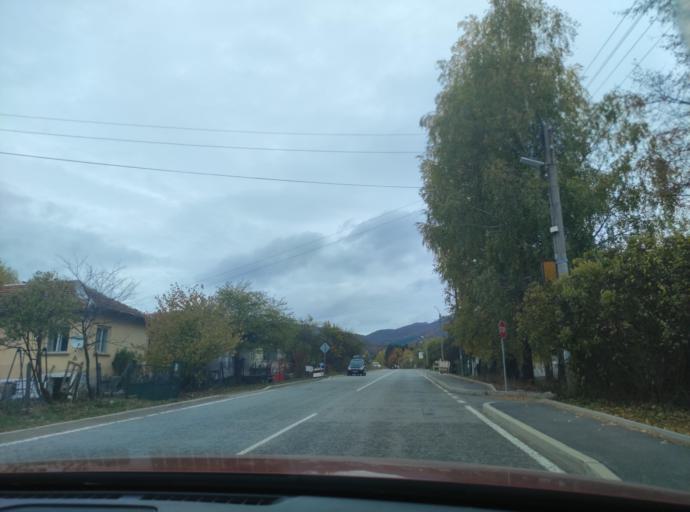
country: BG
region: Sofiya
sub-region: Obshtina Godech
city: Godech
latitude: 43.0956
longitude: 23.0998
